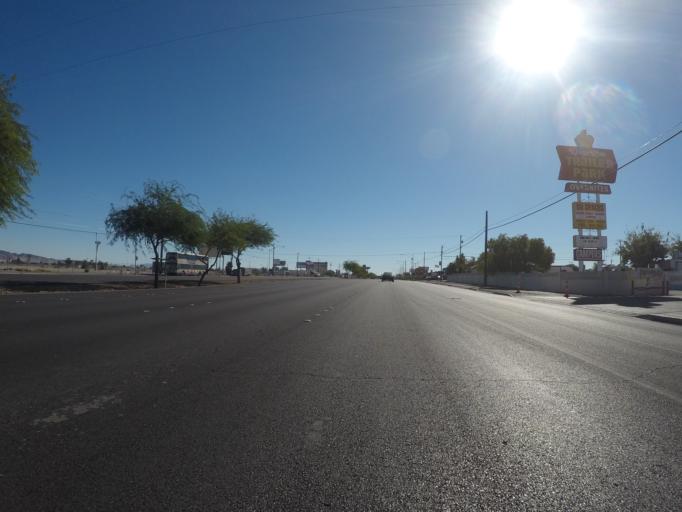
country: US
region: Nevada
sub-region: Clark County
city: Winchester
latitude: 36.1404
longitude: -115.0957
